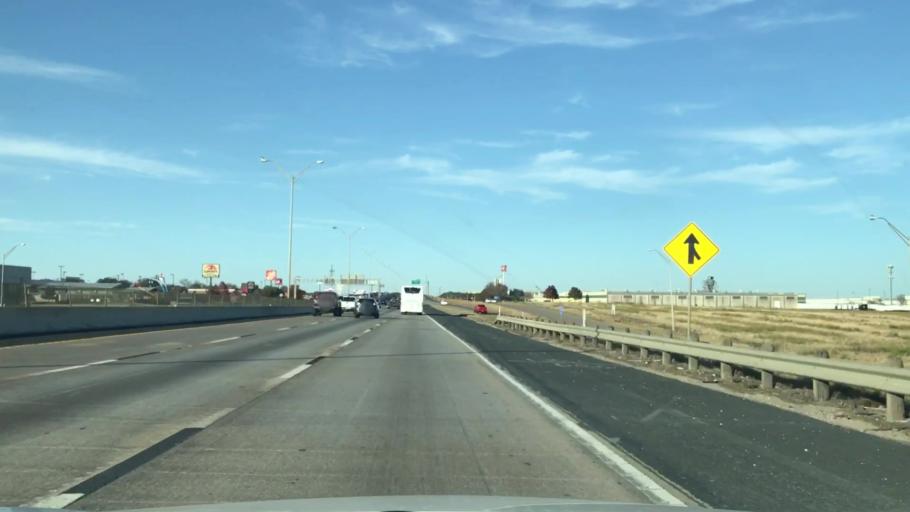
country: US
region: Texas
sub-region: Tarrant County
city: Everman
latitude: 32.6290
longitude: -97.3214
